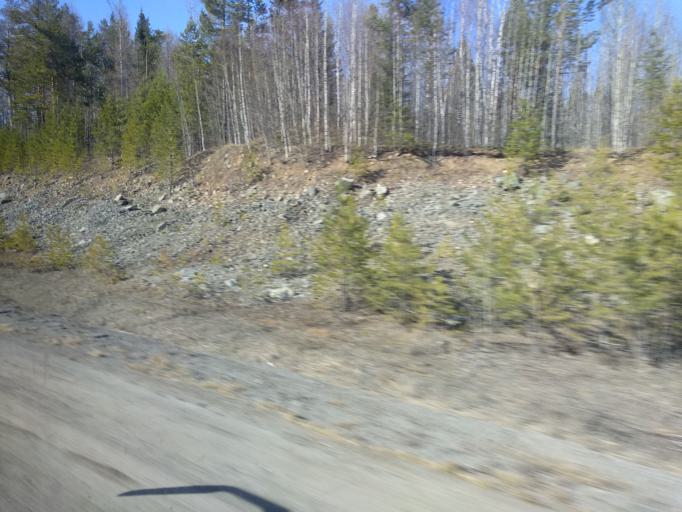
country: RU
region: Sverdlovsk
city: Krasnotur'insk
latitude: 59.6678
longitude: 60.1904
